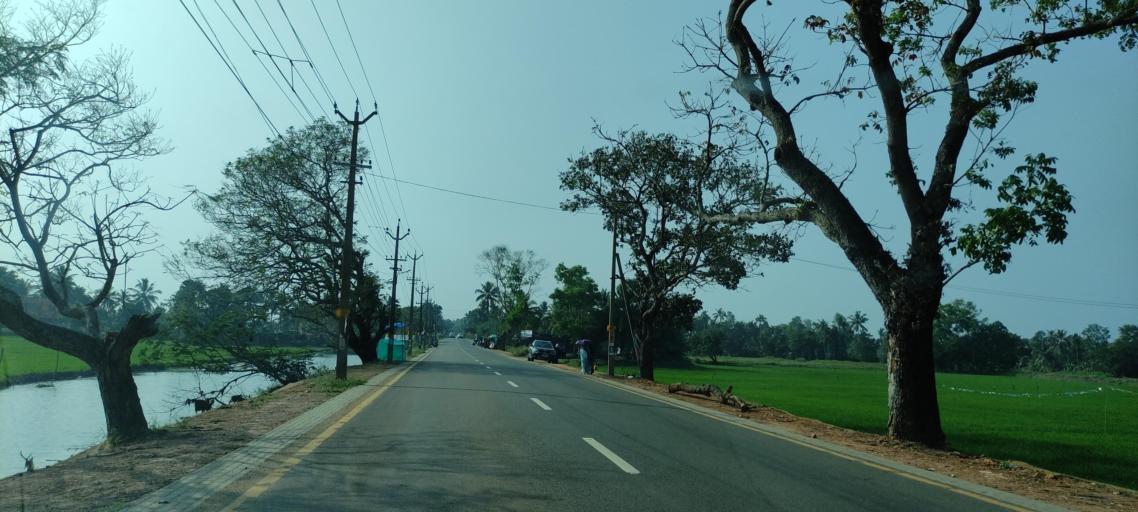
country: IN
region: Kerala
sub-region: Kottayam
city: Changanacheri
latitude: 9.3675
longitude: 76.4328
